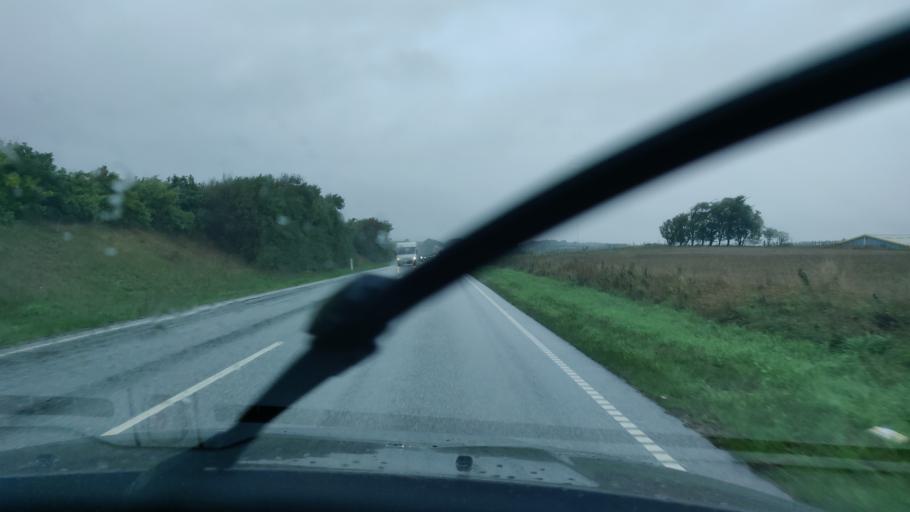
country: DK
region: North Denmark
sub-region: Thisted Kommune
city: Thisted
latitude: 56.9540
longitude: 8.6430
